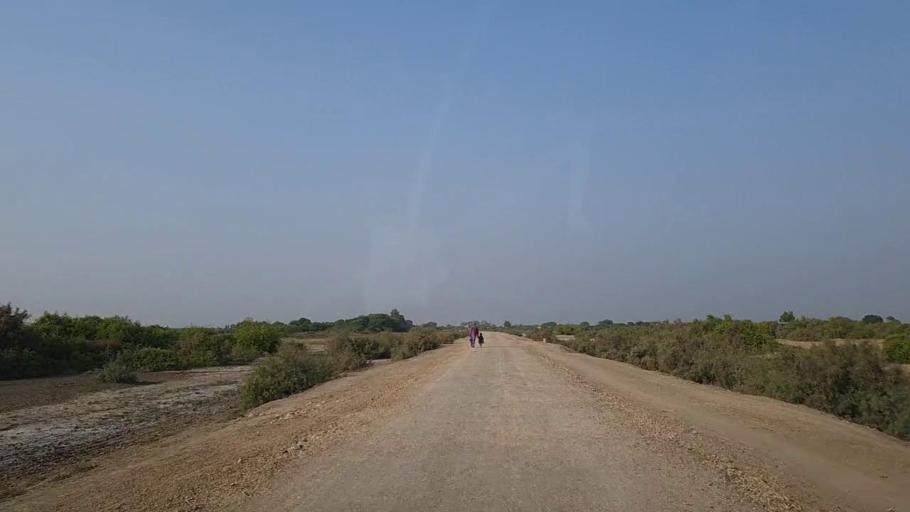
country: PK
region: Sindh
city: Mirpur Sakro
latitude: 24.6404
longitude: 67.7675
